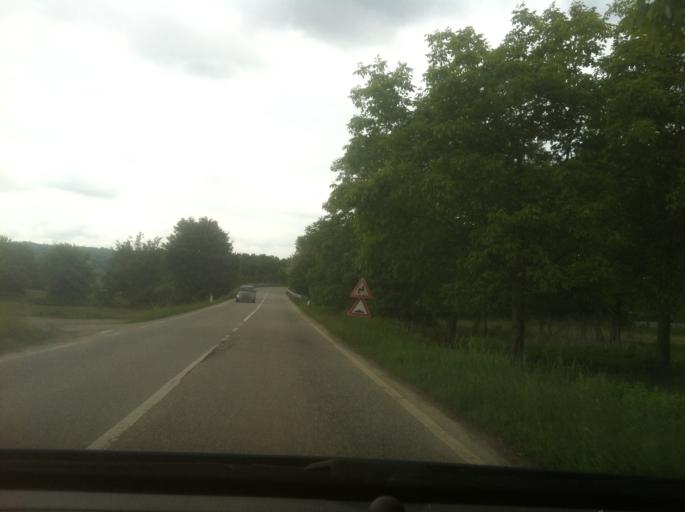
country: IT
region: Piedmont
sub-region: Provincia di Torino
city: Romano Canavese
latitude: 45.4132
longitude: 7.8503
